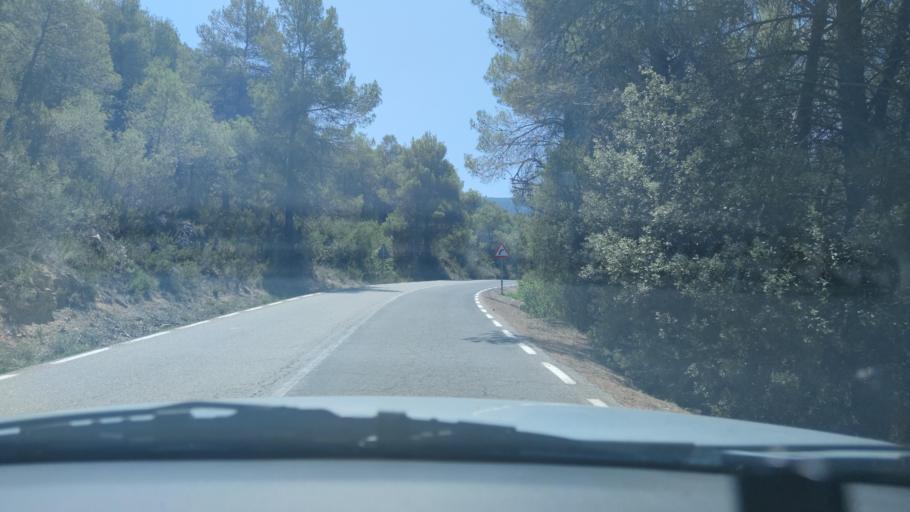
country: ES
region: Catalonia
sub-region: Provincia de Tarragona
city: Vilanova de Prades
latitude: 41.3762
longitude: 0.9394
